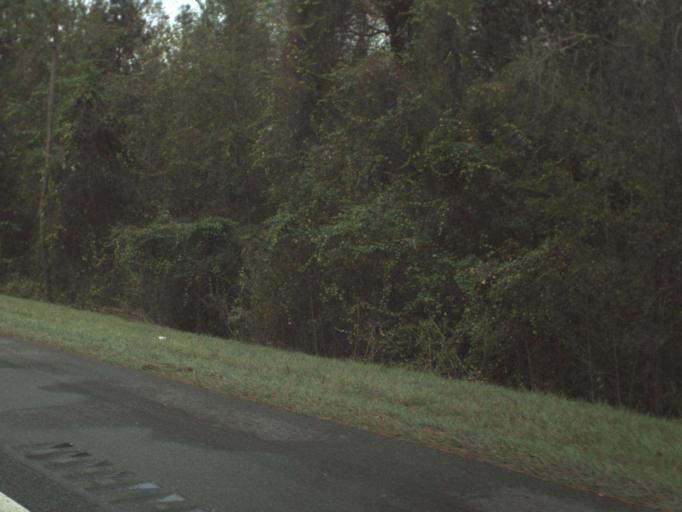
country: US
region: Florida
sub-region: Gadsden County
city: Midway
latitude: 30.5136
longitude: -84.4736
